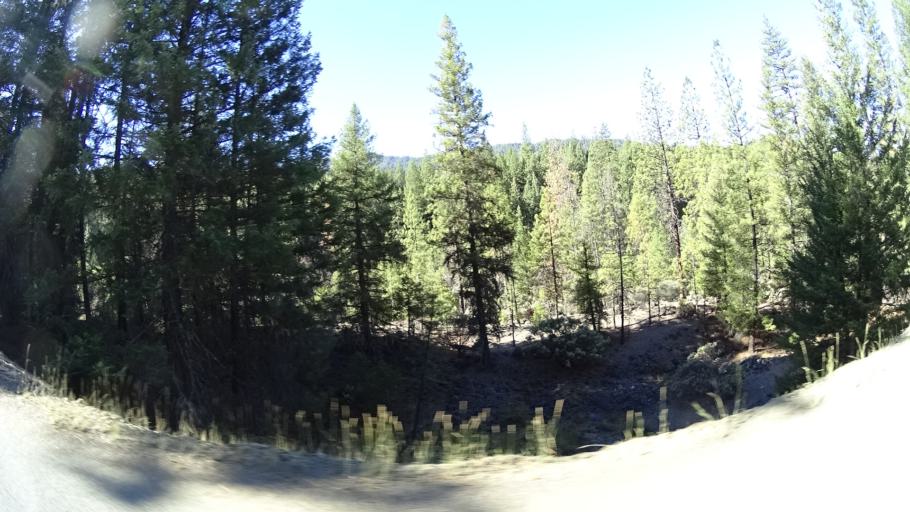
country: US
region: California
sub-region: Trinity County
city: Weaverville
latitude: 41.1153
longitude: -123.0901
